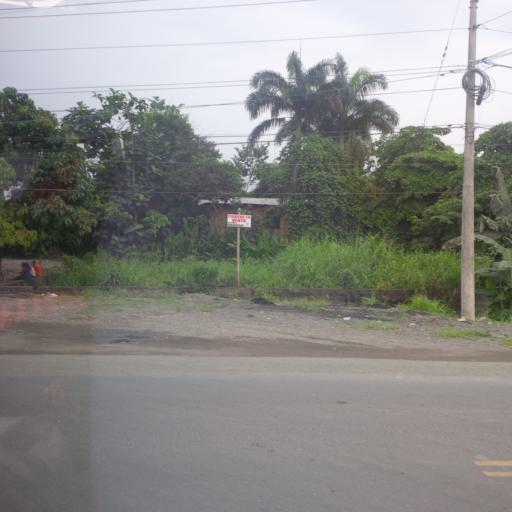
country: EC
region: Canar
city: La Troncal
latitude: -2.3358
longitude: -79.3986
